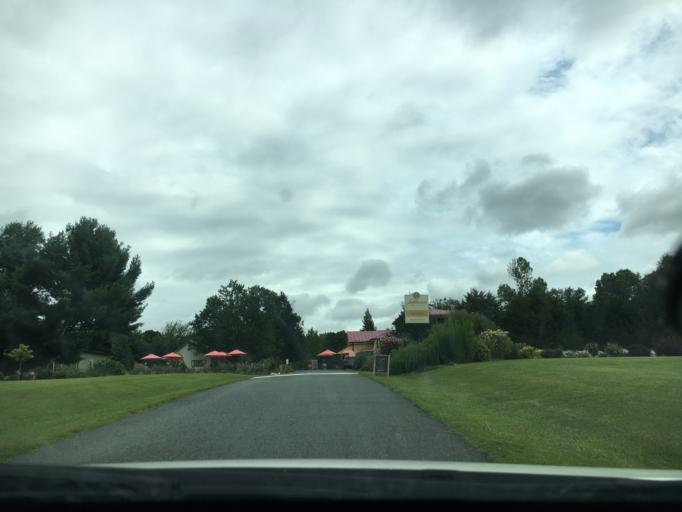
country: US
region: Virginia
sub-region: City of Charlottesville
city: Charlottesville
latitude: 37.9907
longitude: -78.4444
